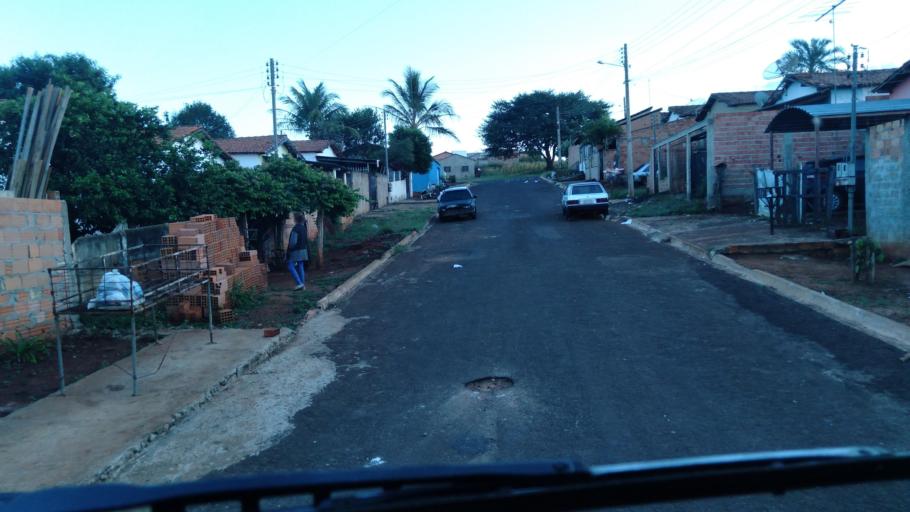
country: BR
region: Goias
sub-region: Mineiros
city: Mineiros
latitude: -17.5713
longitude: -52.5712
